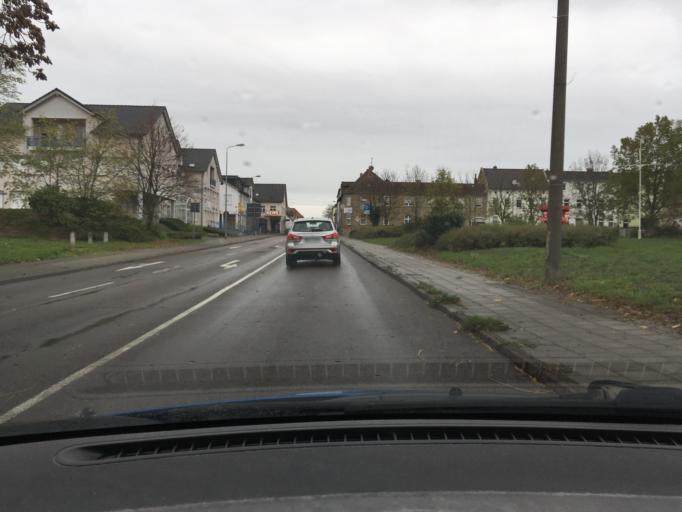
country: DE
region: Saxony-Anhalt
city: Rosslau
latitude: 51.8832
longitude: 12.2401
